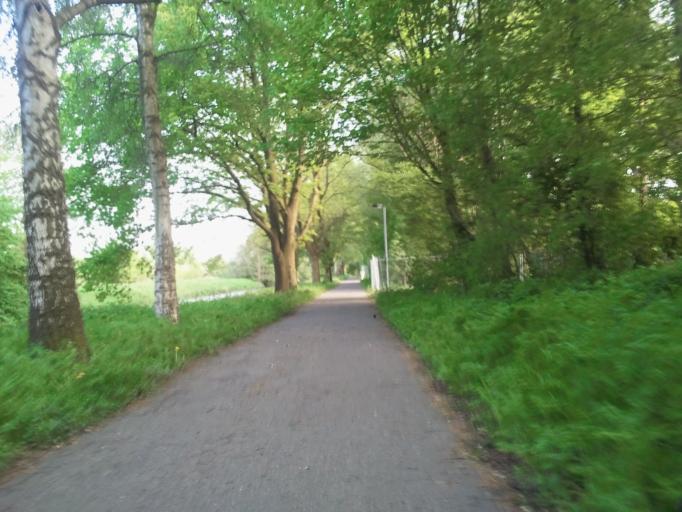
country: DE
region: Lower Saxony
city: Nienburg
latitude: 52.6388
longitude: 9.2290
